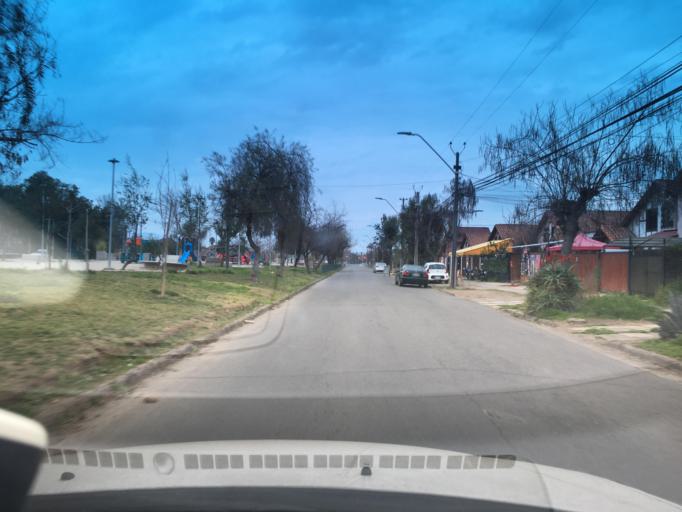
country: CL
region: Santiago Metropolitan
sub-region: Provincia de Santiago
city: Villa Presidente Frei, Nunoa, Santiago, Chile
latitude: -33.4998
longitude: -70.6054
